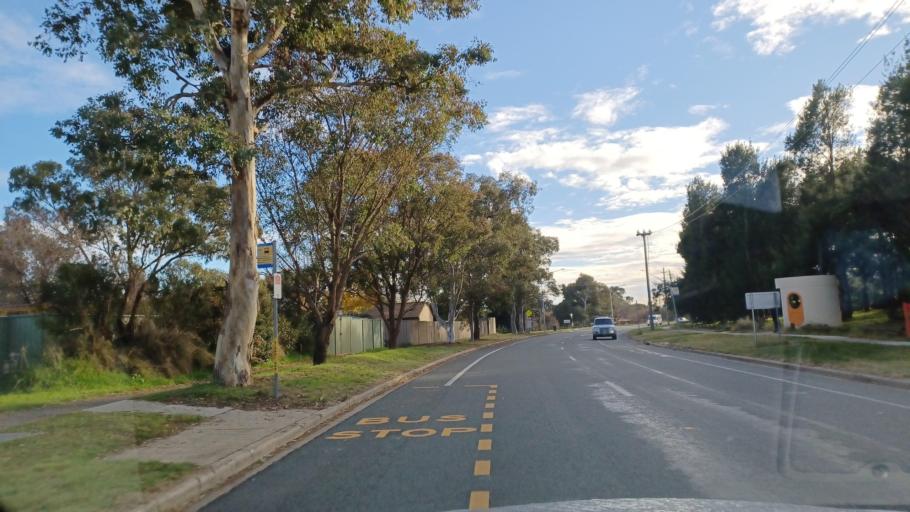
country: AU
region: Australian Capital Territory
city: Belconnen
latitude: -35.1953
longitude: 149.0415
